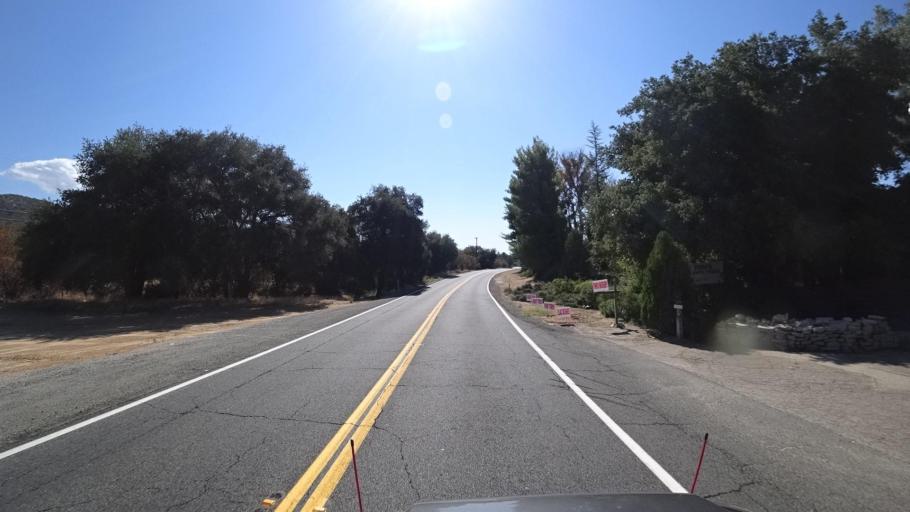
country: US
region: California
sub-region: Riverside County
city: Aguanga
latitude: 33.3480
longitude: -116.7319
